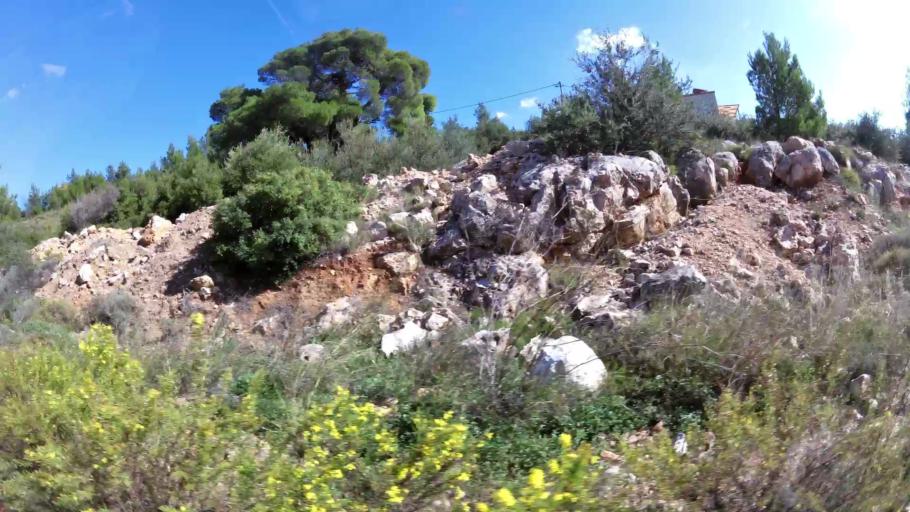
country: GR
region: Attica
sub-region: Nomarchia Anatolikis Attikis
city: Dioni
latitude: 38.0303
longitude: 23.9212
